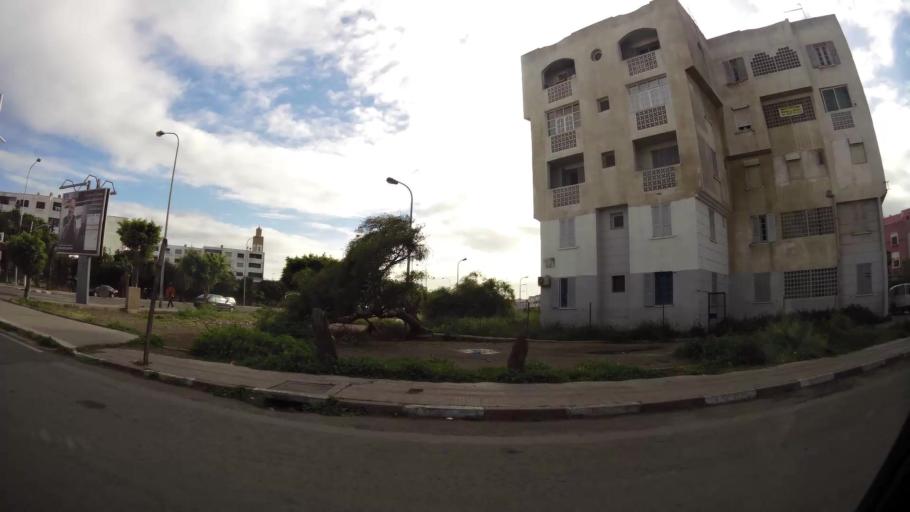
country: MA
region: Doukkala-Abda
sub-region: El-Jadida
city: El Jadida
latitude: 33.2423
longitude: -8.5249
